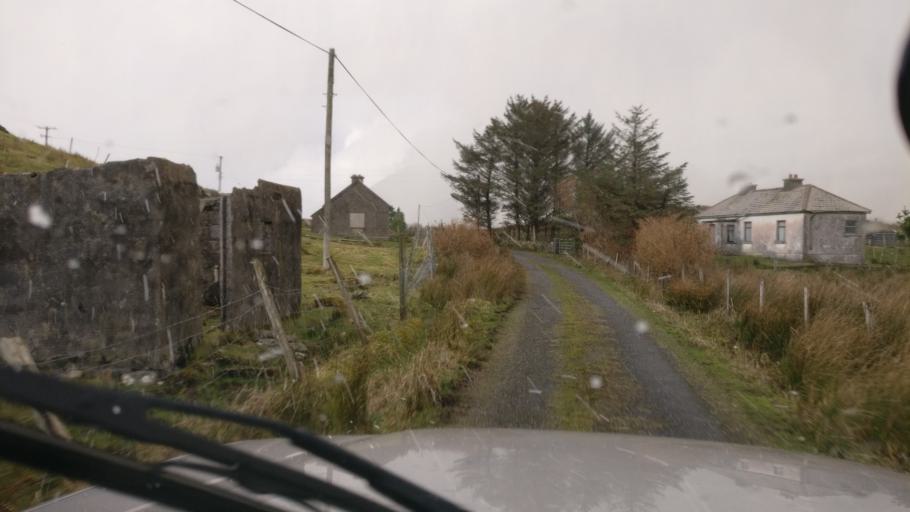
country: IE
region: Connaught
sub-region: County Galway
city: Clifden
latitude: 53.4886
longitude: -9.6984
